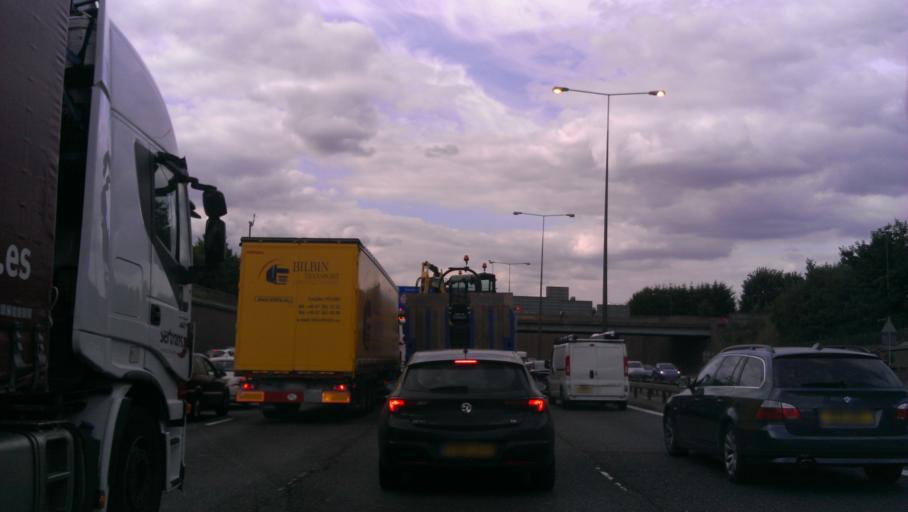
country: GB
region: England
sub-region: Kent
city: Dartford
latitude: 51.4395
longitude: 0.2387
